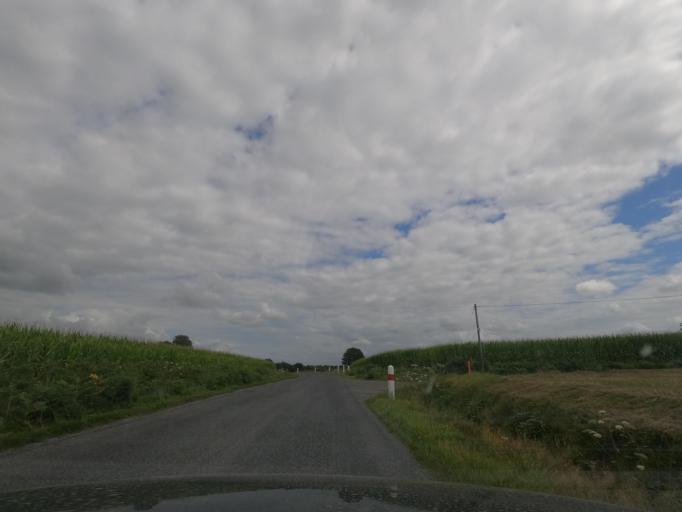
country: FR
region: Pays de la Loire
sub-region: Departement de la Mayenne
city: Fougerolles-du-Plessis
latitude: 48.4933
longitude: -0.9366
